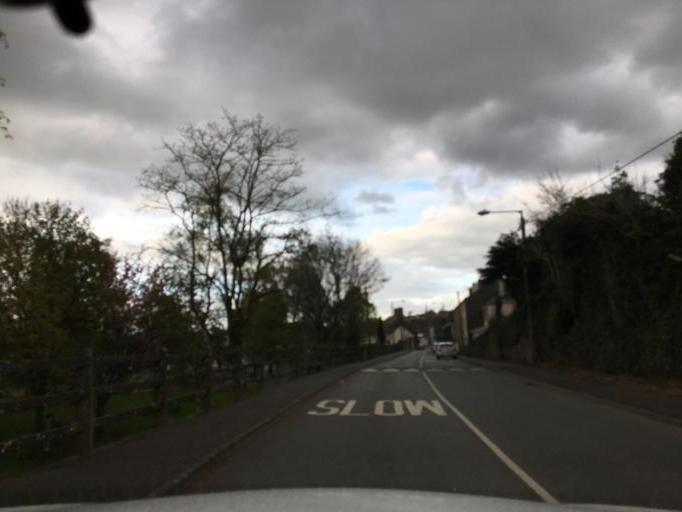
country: IE
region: Leinster
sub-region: Loch Garman
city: New Ross
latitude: 52.3898
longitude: -6.9487
